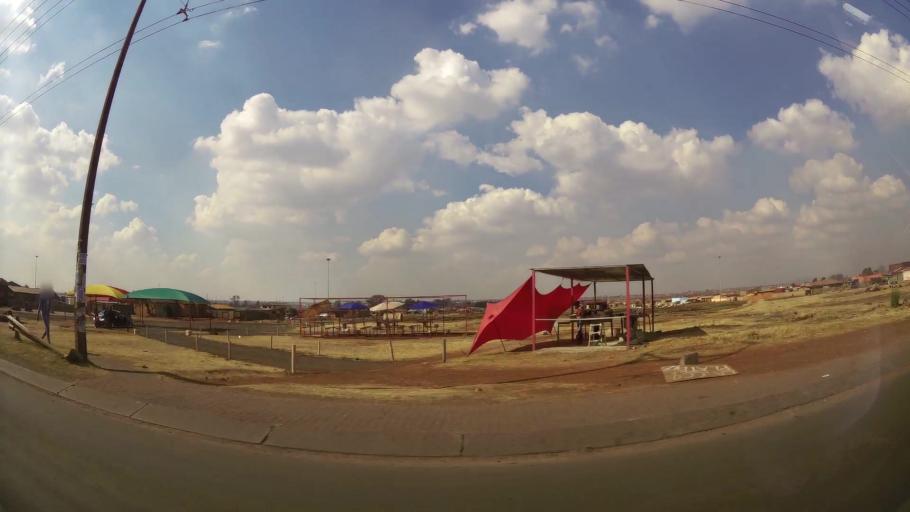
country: ZA
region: Gauteng
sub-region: Ekurhuleni Metropolitan Municipality
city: Germiston
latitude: -26.3519
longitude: 28.1620
